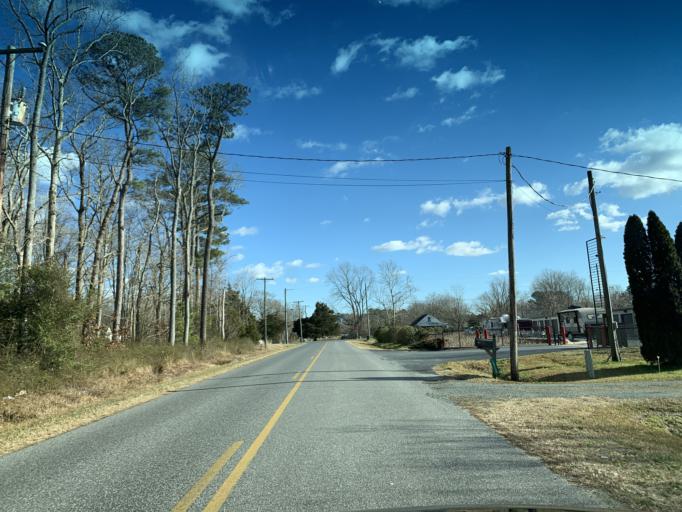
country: US
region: Maryland
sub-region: Worcester County
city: Berlin
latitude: 38.3661
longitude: -75.2024
